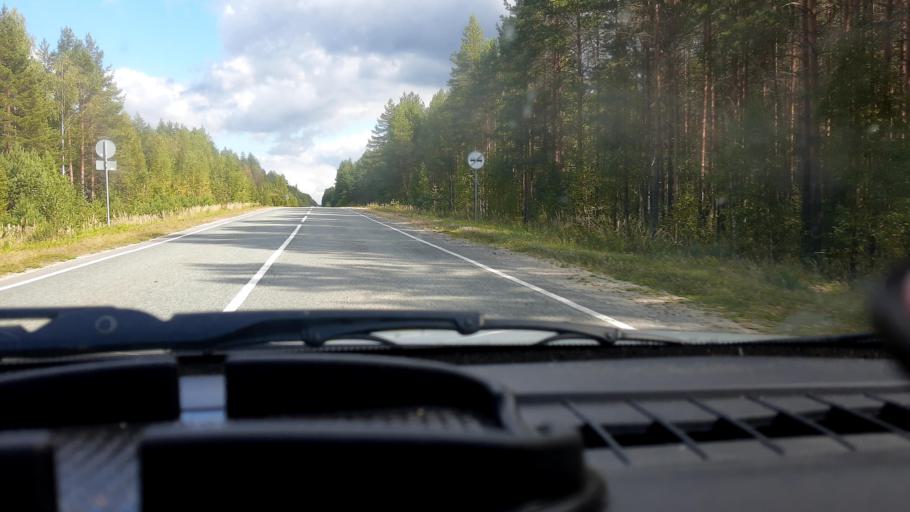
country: RU
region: Mariy-El
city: Medvedevo
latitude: 56.5739
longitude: 47.4362
